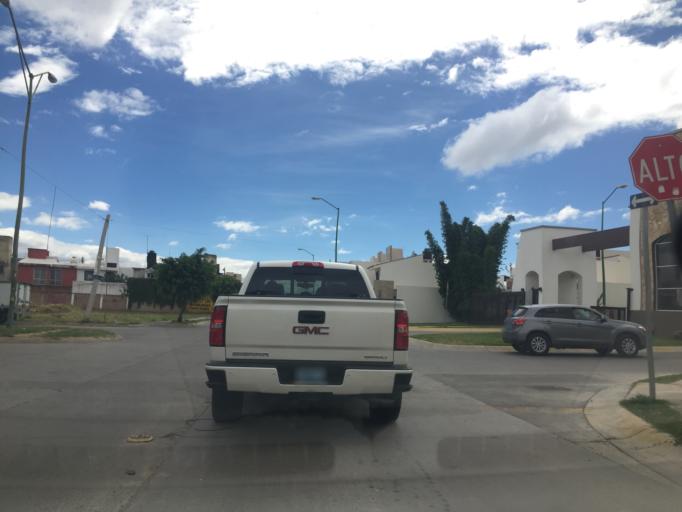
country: MX
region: Guanajuato
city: Leon
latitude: 21.1524
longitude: -101.6608
